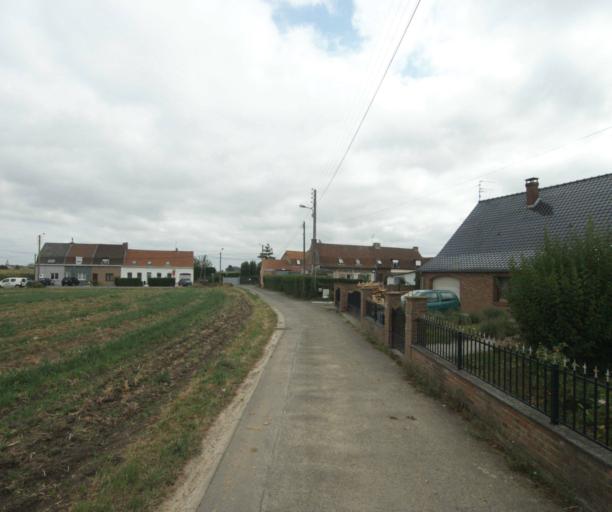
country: FR
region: Nord-Pas-de-Calais
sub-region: Departement du Nord
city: Leers
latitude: 50.6726
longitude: 3.2478
